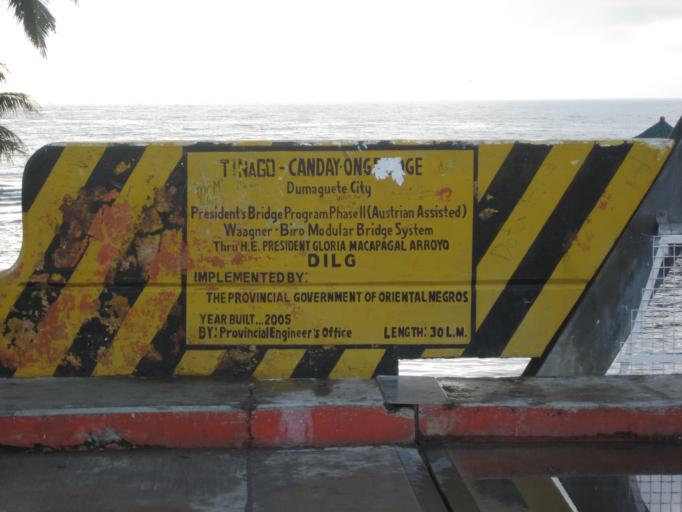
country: PH
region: Central Visayas
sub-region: Province of Negros Oriental
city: Dumaguete
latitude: 9.3017
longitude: 123.3107
